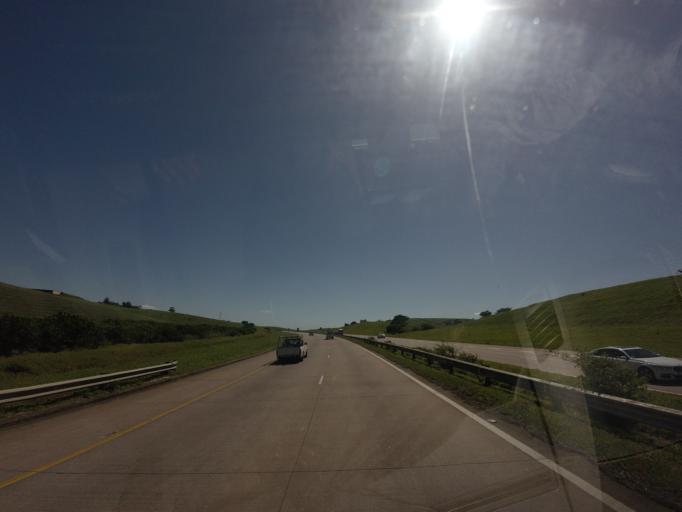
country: ZA
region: KwaZulu-Natal
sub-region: iLembe District Municipality
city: Stanger
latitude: -29.4357
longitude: 31.2684
